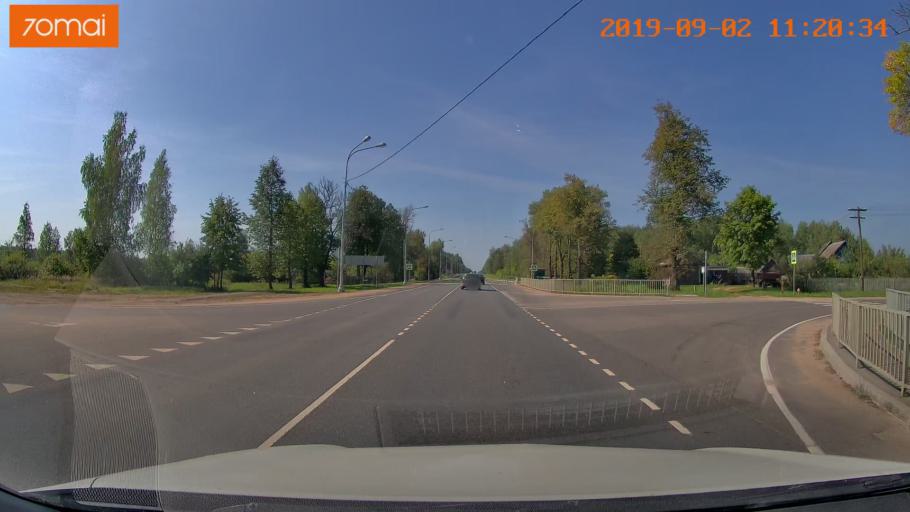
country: RU
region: Smolensk
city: Roslavl'
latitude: 54.0412
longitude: 33.0512
